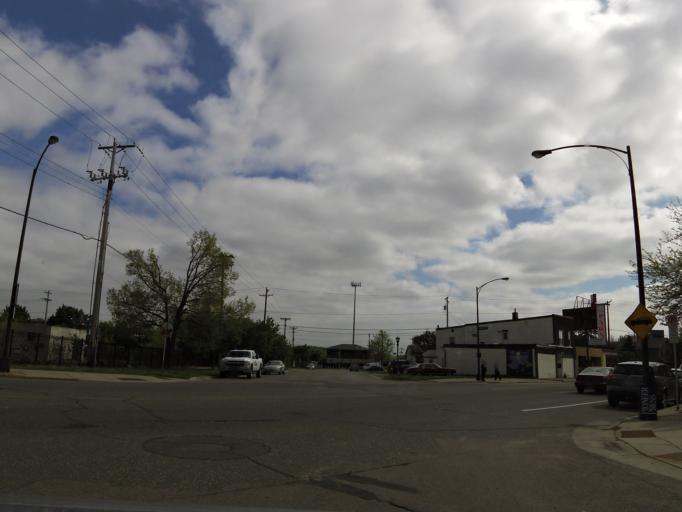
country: US
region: Minnesota
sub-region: Dakota County
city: West Saint Paul
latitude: 44.9286
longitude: -93.1258
